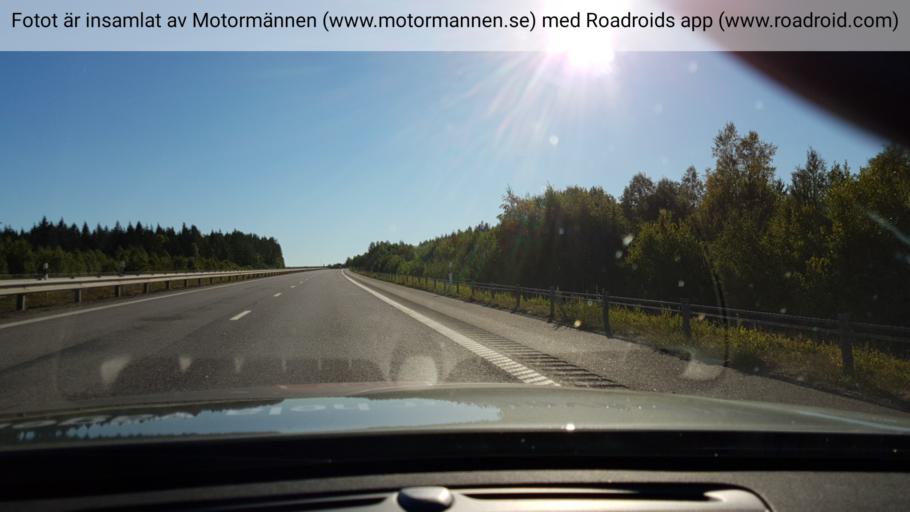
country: SE
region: Vaestmanland
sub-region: Arboga Kommun
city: Arboga
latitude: 59.4023
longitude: 15.7367
